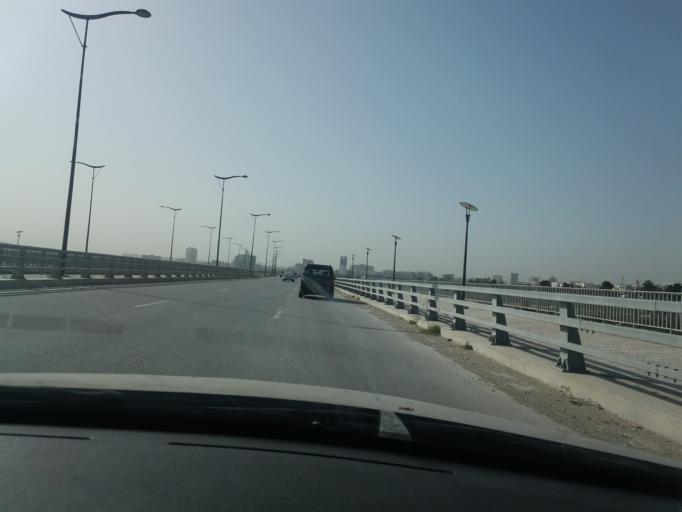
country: TN
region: Tunis
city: Tunis
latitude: 36.8206
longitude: 10.1999
